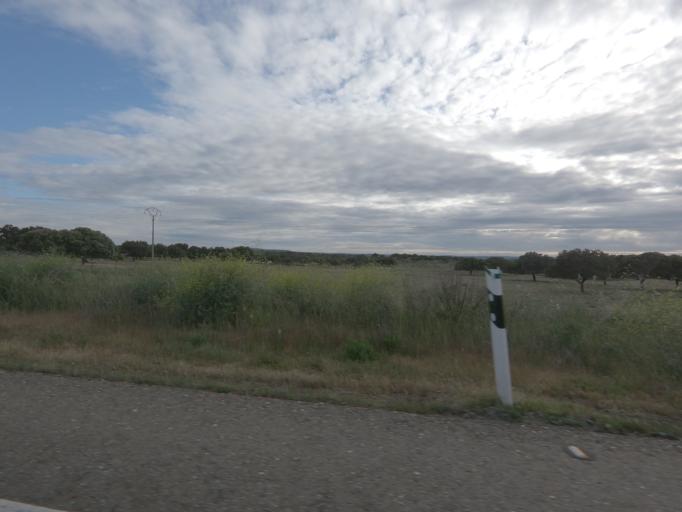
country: ES
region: Extremadura
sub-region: Provincia de Caceres
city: Torrejoncillo
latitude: 39.9218
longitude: -6.4947
